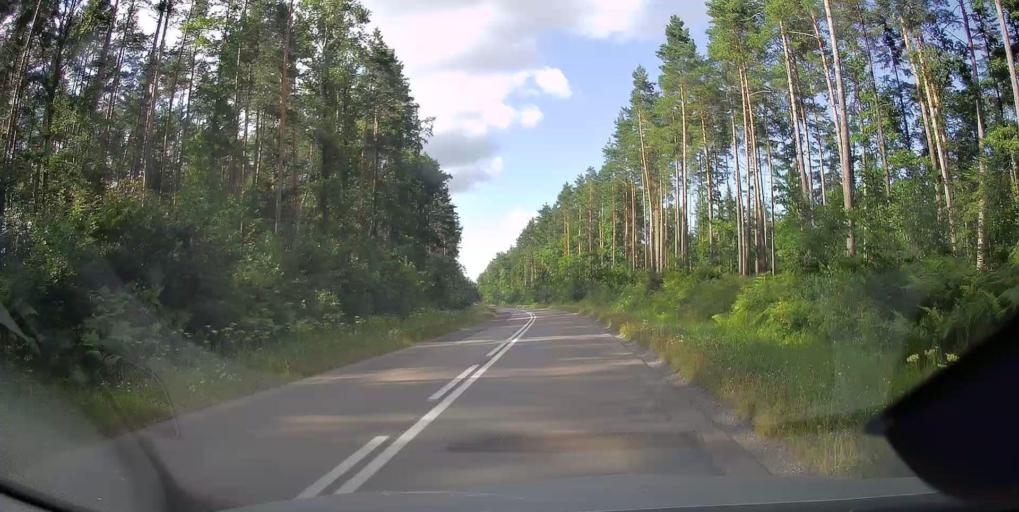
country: PL
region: Swietokrzyskie
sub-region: Powiat skarzyski
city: Suchedniow
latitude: 51.0162
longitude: 20.8397
